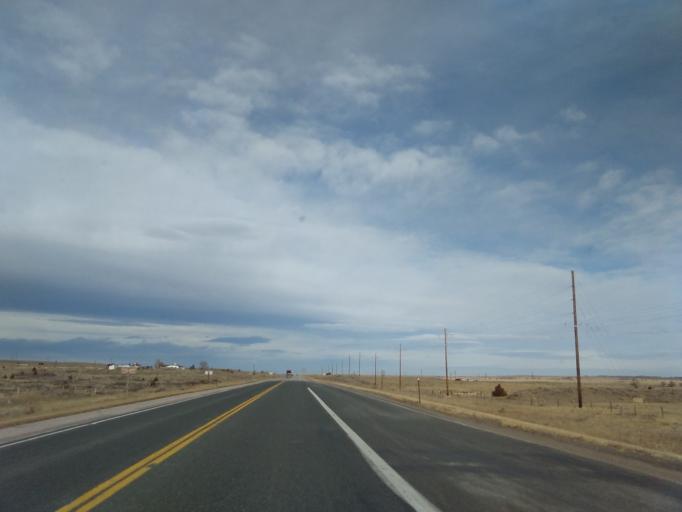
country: US
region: Wyoming
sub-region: Goshen County
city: Torrington
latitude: 41.6461
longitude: -104.2407
